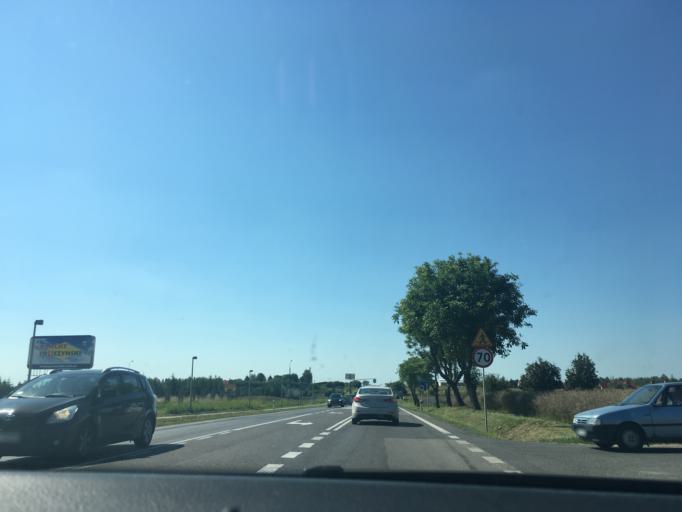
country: PL
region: Lublin Voivodeship
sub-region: Powiat lubelski
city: Niemce
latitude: 51.3446
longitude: 22.6191
